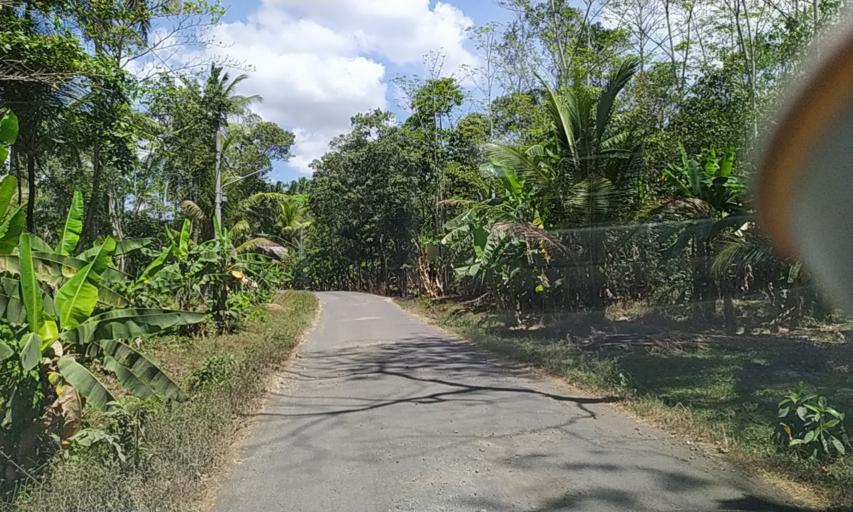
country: ID
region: Central Java
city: Cinyawang
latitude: -7.5773
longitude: 108.7681
